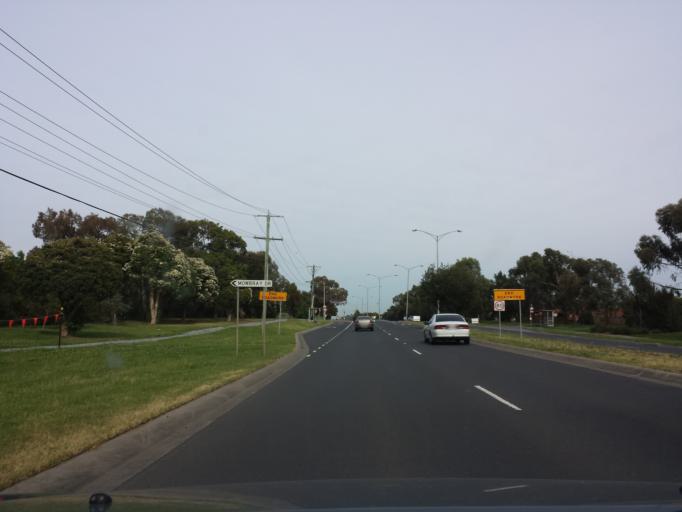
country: AU
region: Victoria
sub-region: Knox
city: Wantirna South
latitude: -37.8770
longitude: 145.2267
